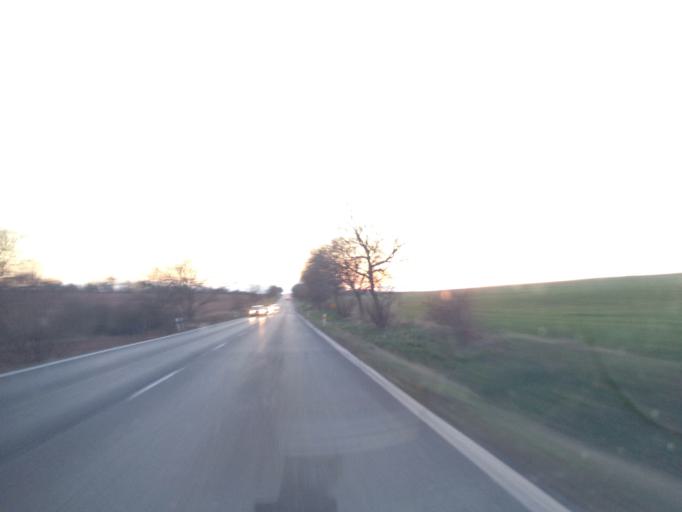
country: CZ
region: Ustecky
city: Mecholupy
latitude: 50.1615
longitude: 13.5825
